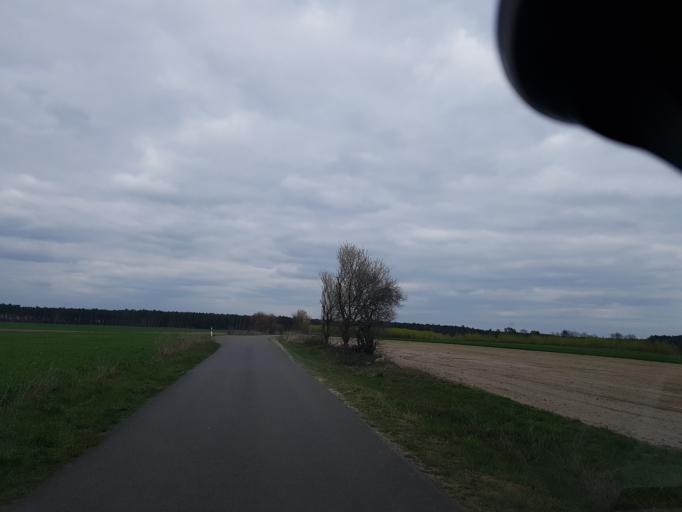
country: DE
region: Brandenburg
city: Linthe
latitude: 52.1191
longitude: 12.7983
